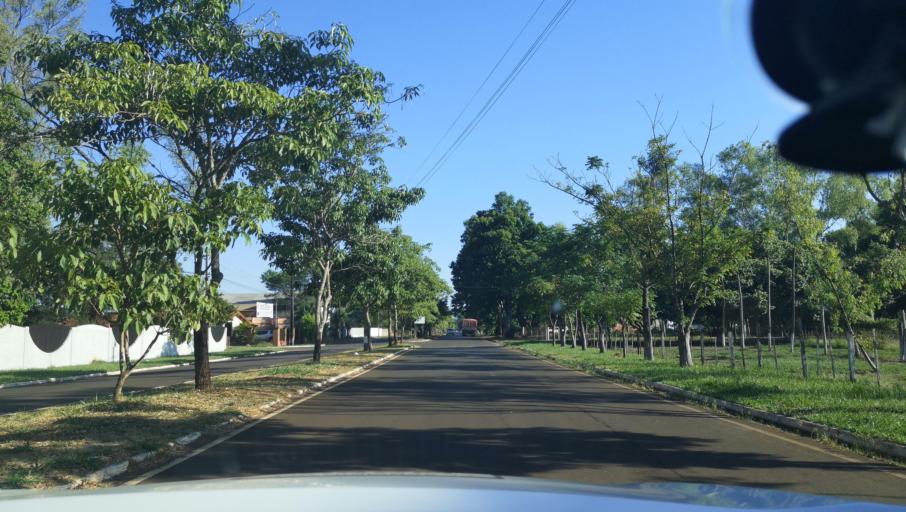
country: PY
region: Itapua
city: Carmen del Parana
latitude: -27.1622
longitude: -56.2420
